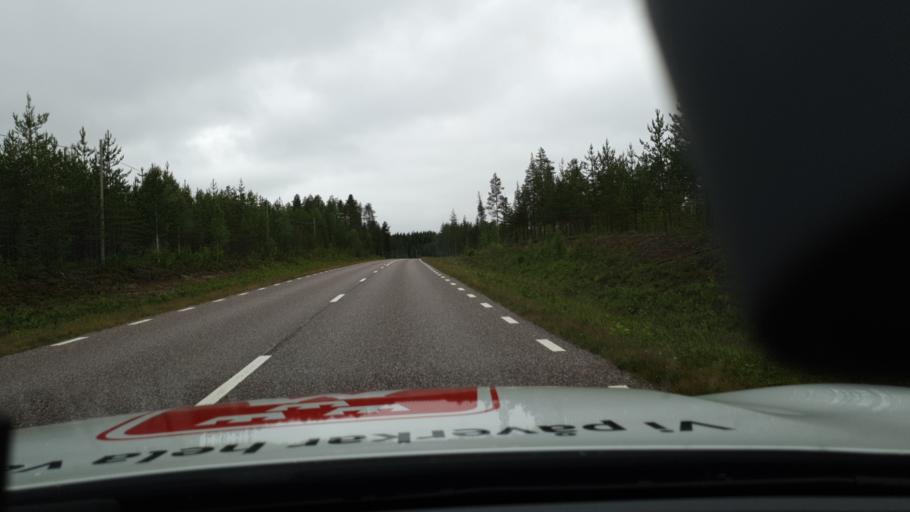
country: FI
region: Lapland
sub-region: Tunturi-Lappi
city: Kolari
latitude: 67.0422
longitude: 23.6909
